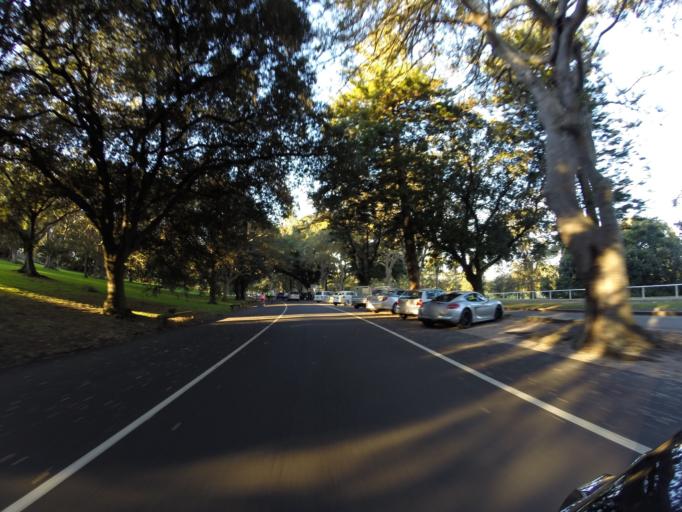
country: AU
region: New South Wales
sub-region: Woollahra
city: Woollahra
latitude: -33.8970
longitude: 151.2298
